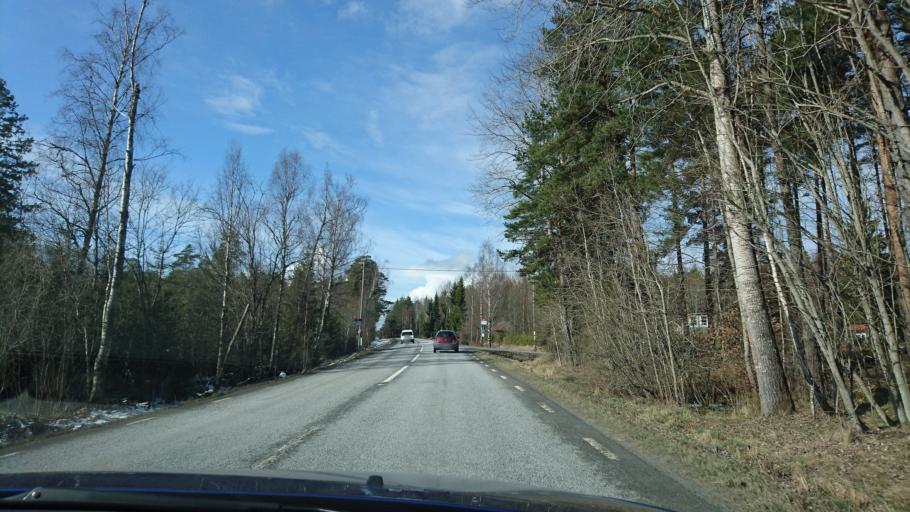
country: SE
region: Stockholm
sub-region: Norrtalje Kommun
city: Norrtalje
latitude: 59.7757
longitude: 18.7544
